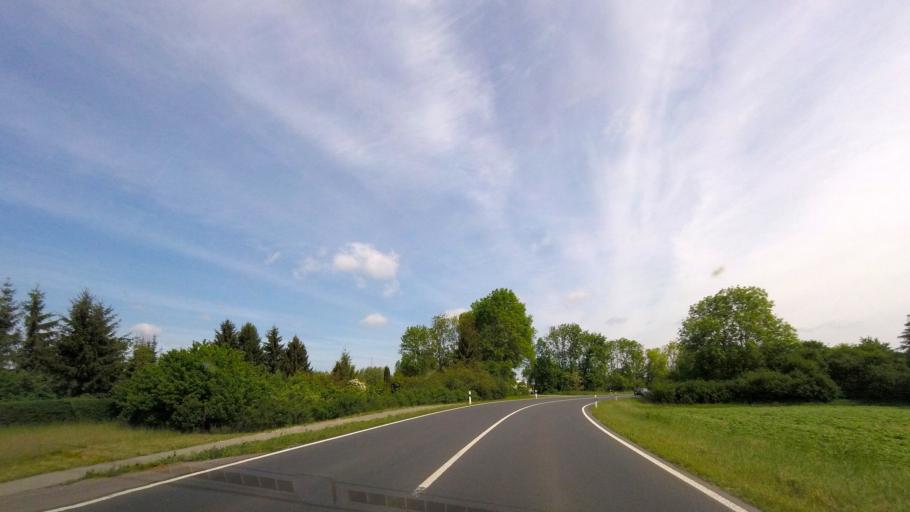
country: DE
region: Brandenburg
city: Wittstock
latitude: 53.1586
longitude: 12.4955
